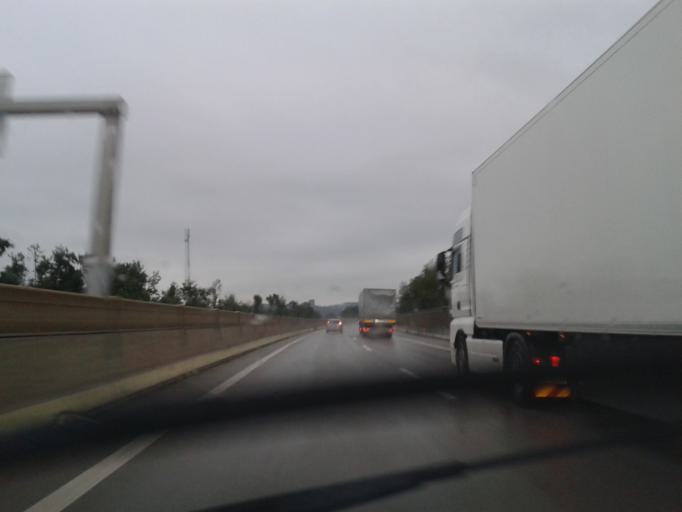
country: AT
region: Styria
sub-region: Politischer Bezirk Weiz
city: Gleisdorf
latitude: 47.0993
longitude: 15.6915
